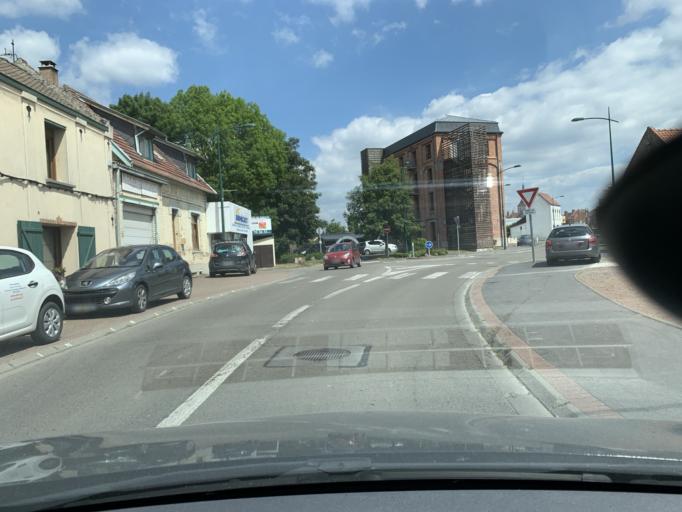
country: FR
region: Nord-Pas-de-Calais
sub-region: Departement du Nord
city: Arleux
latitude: 50.2778
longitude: 3.1012
